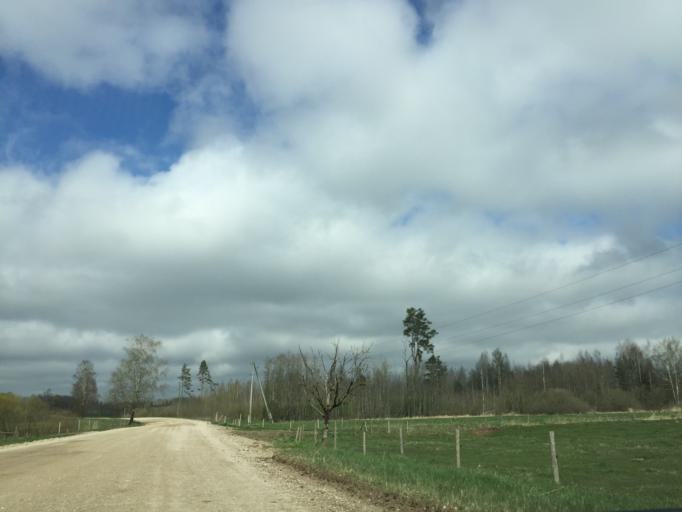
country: EE
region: Valgamaa
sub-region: Valga linn
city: Valga
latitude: 57.5562
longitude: 26.2818
